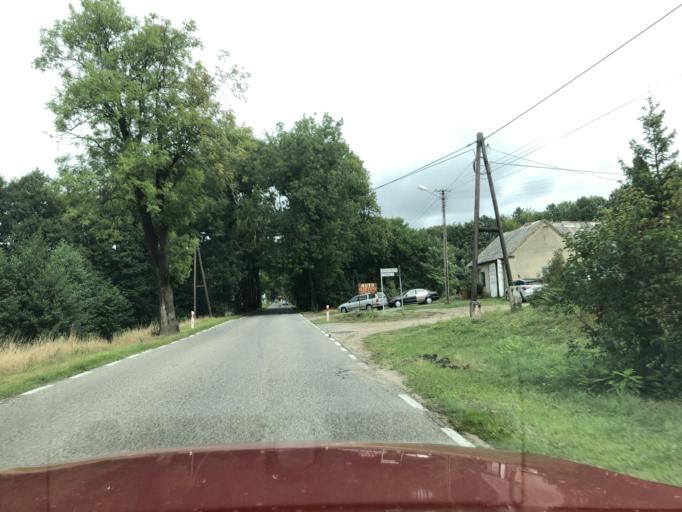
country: PL
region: Greater Poland Voivodeship
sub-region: Powiat miedzychodzki
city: Chrzypsko Wielkie
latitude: 52.6008
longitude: 16.3100
